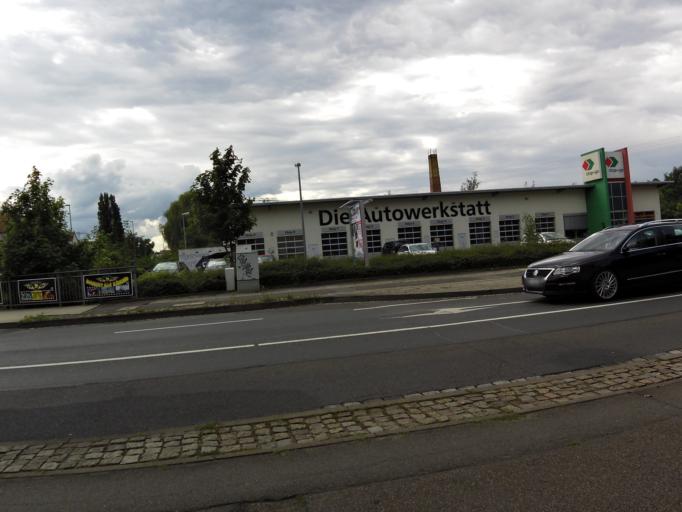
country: DE
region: Saxony
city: Leipzig
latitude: 51.3540
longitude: 12.3964
